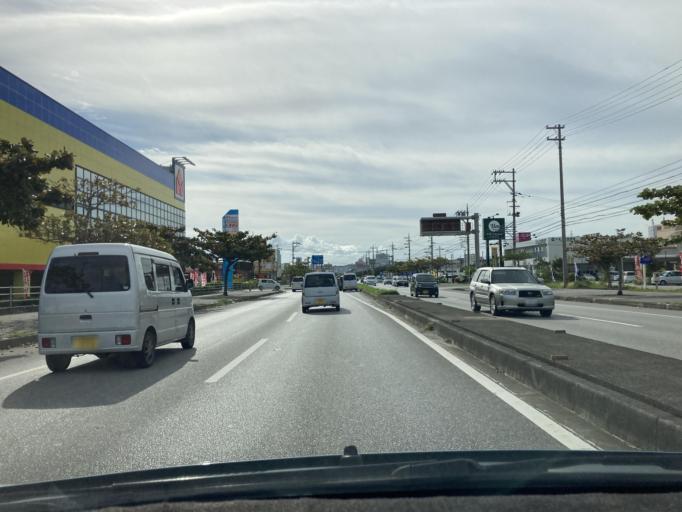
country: JP
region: Okinawa
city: Katsuren-haebaru
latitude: 26.3390
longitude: 127.8486
